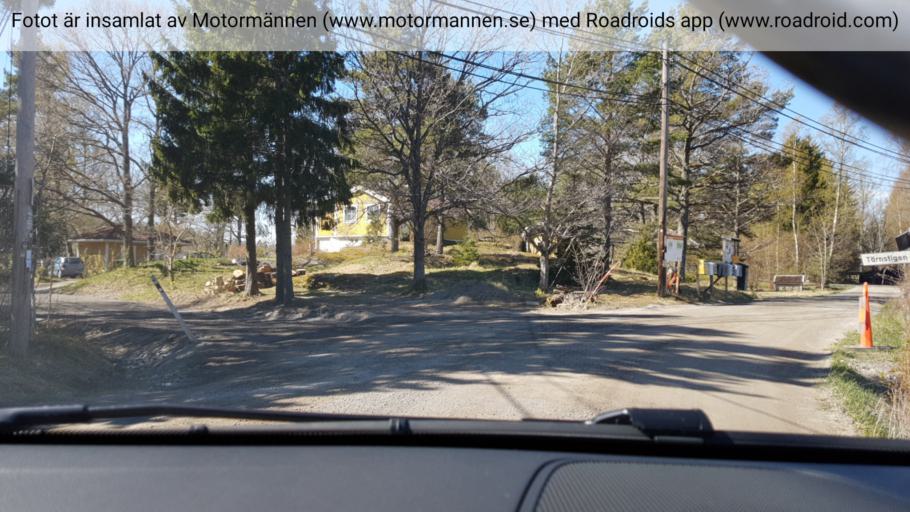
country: SE
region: Stockholm
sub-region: Varmdo Kommun
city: Hemmesta
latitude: 59.2890
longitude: 18.5452
